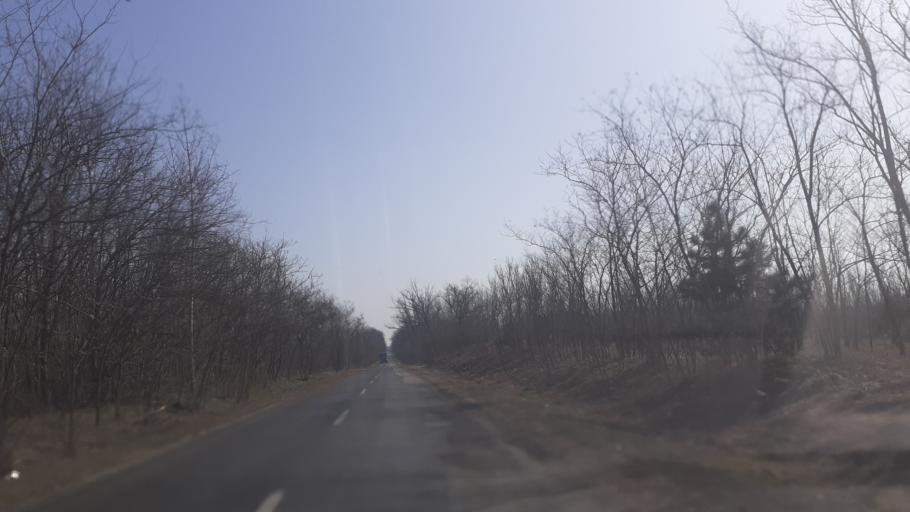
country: HU
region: Pest
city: Orkeny
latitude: 47.0700
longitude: 19.3865
